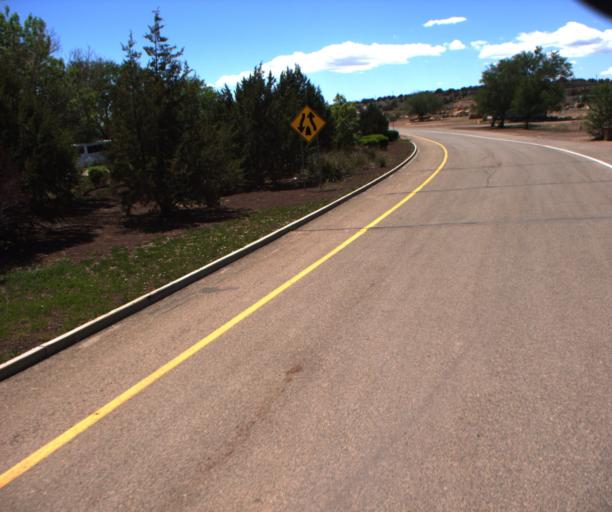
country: US
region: Arizona
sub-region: Coconino County
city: Williams
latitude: 35.2249
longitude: -112.4893
